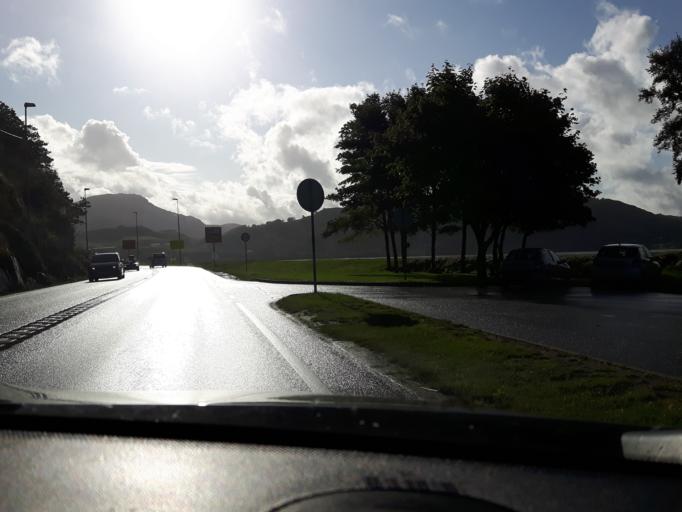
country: NO
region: Rogaland
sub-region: Gjesdal
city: Algard
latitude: 58.7659
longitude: 5.8726
